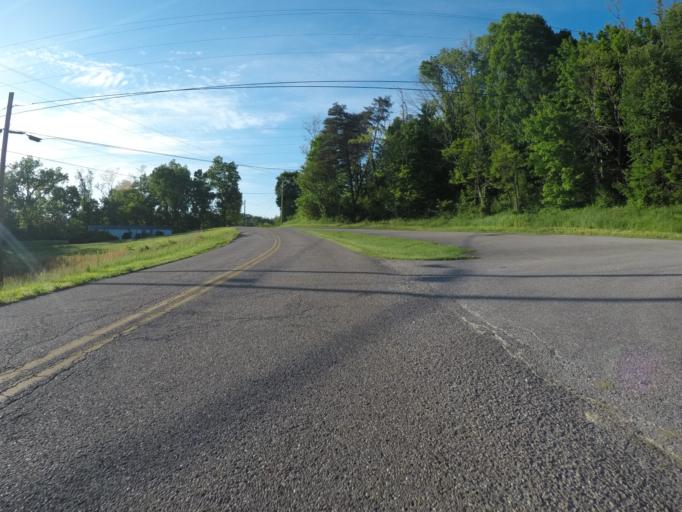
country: US
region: West Virginia
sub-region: Cabell County
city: Huntington
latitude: 38.5300
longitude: -82.4237
